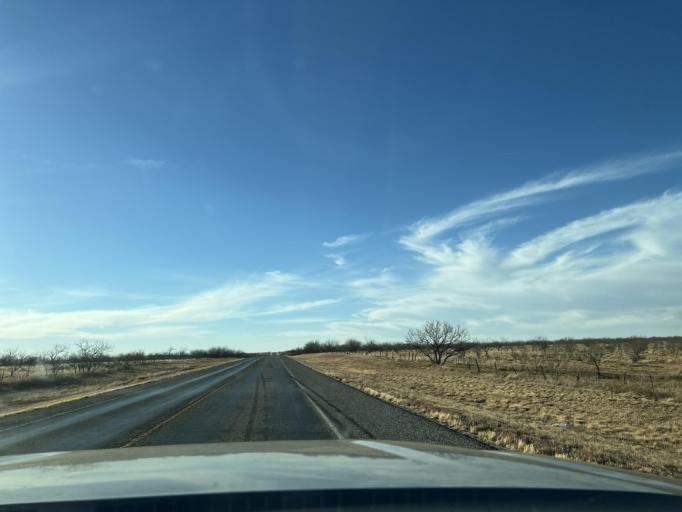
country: US
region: Texas
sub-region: Borden County
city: Gail
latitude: 32.7549
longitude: -101.2391
